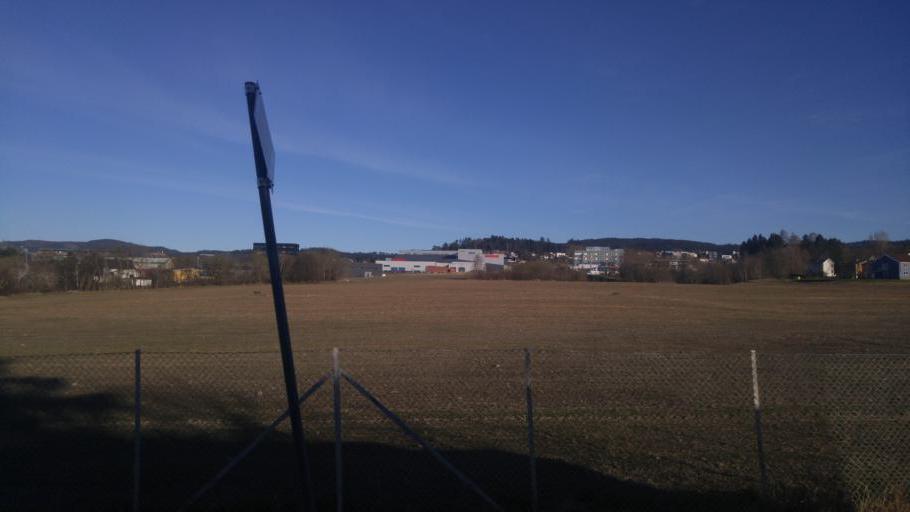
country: NO
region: Sor-Trondelag
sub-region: Trondheim
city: Trondheim
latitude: 63.4240
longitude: 10.4558
